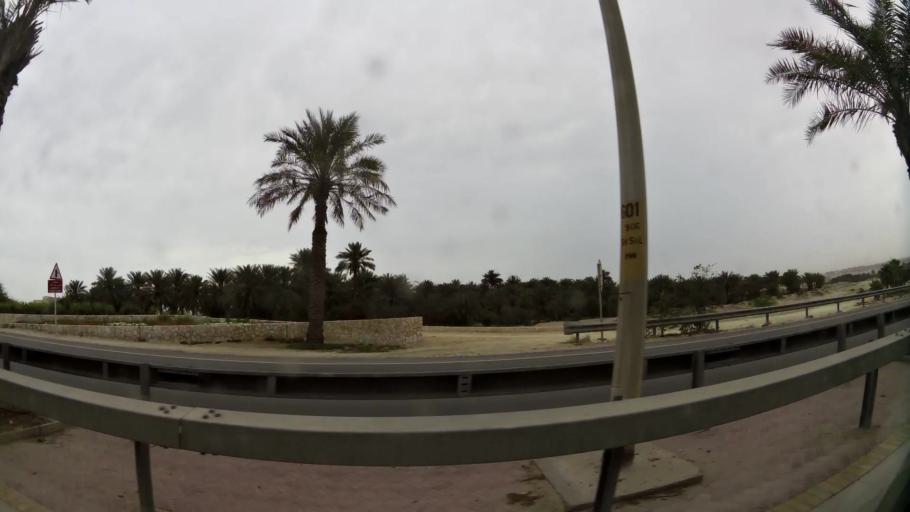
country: BH
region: Northern
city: Ar Rifa'
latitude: 26.1178
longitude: 50.5371
